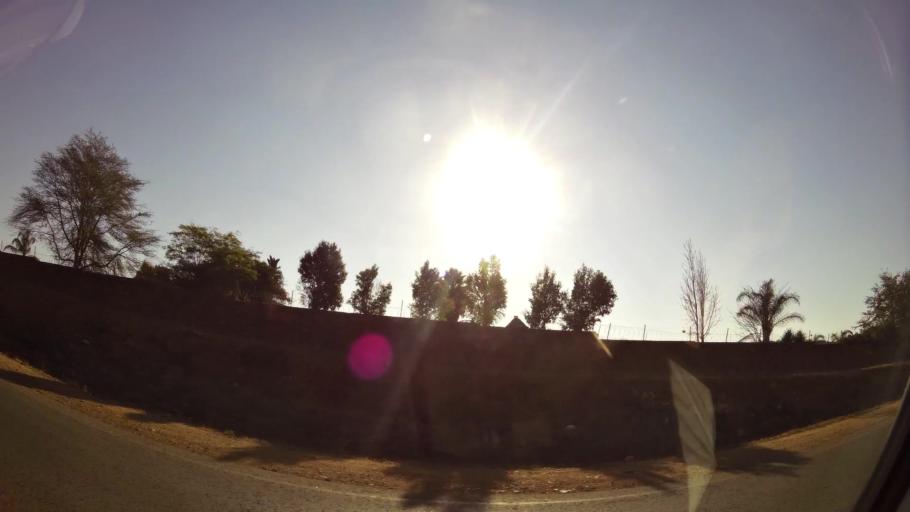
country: ZA
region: Gauteng
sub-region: City of Tshwane Metropolitan Municipality
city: Pretoria
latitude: -25.7851
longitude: 28.3312
